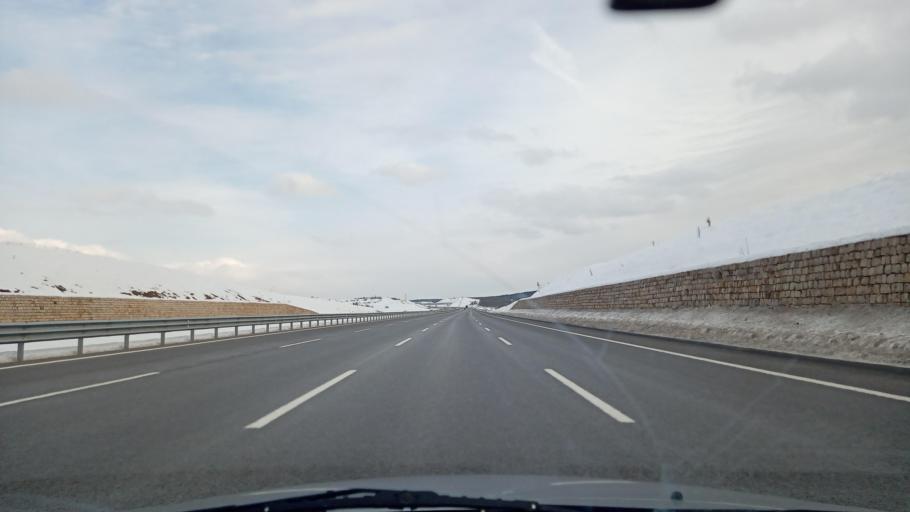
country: TR
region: Kocaeli
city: Hereke
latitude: 40.8929
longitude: 29.6085
